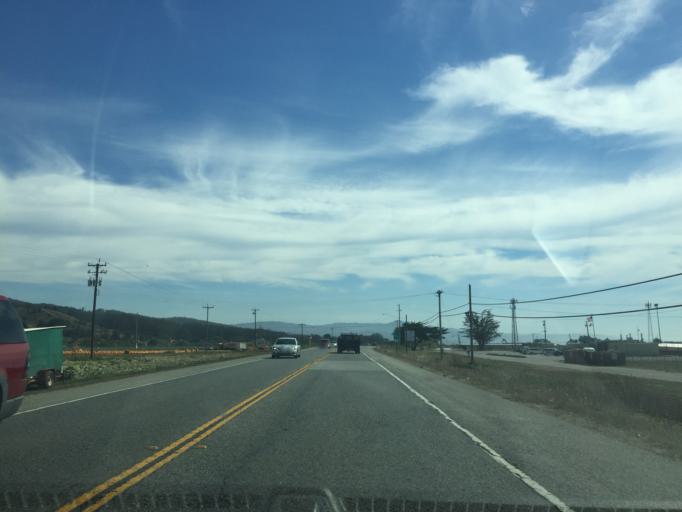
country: US
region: California
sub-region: San Mateo County
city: Moss Beach
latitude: 37.5155
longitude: -122.4962
